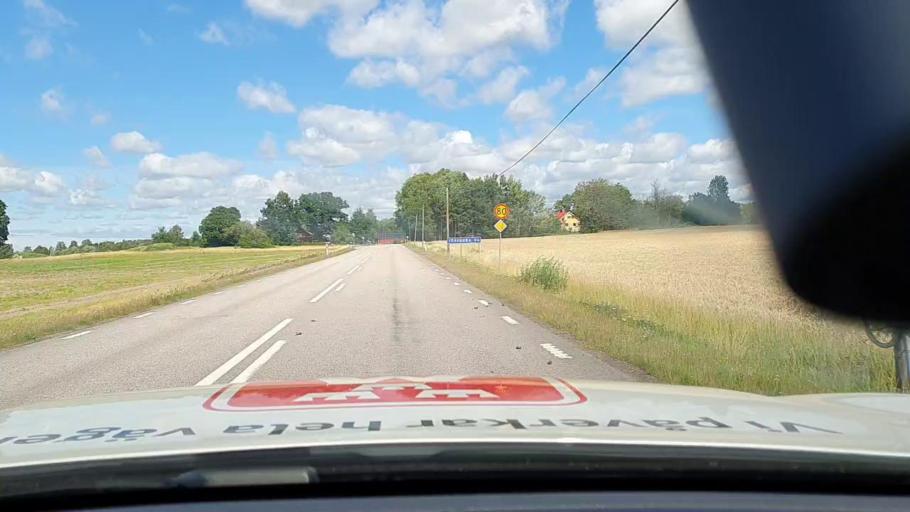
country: SE
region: Vaestra Goetaland
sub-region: Skovde Kommun
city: Stopen
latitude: 58.5125
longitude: 13.9731
